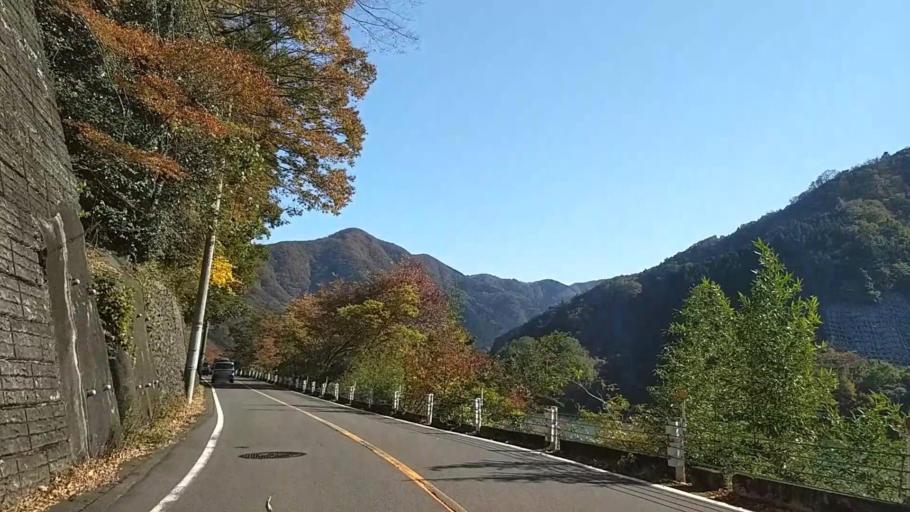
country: JP
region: Yamanashi
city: Uenohara
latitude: 35.7785
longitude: 139.0122
